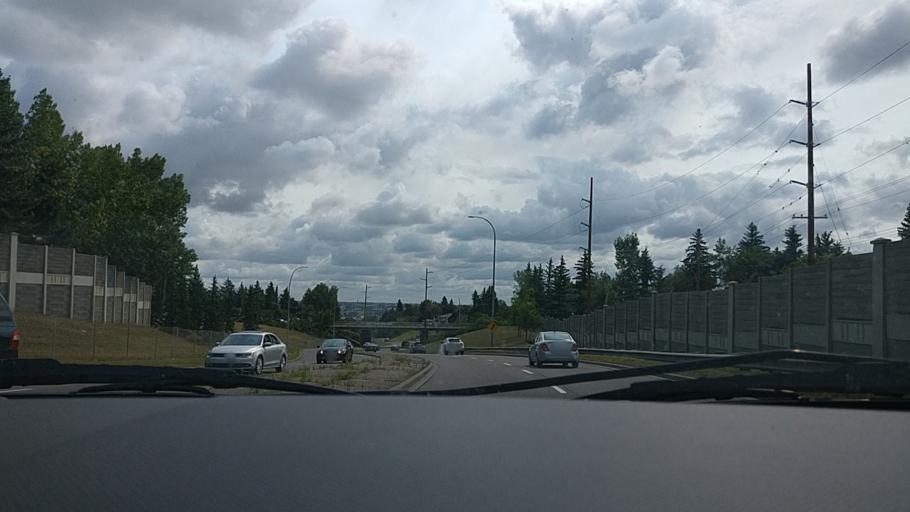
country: CA
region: Alberta
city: Calgary
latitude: 51.0966
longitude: -114.0813
